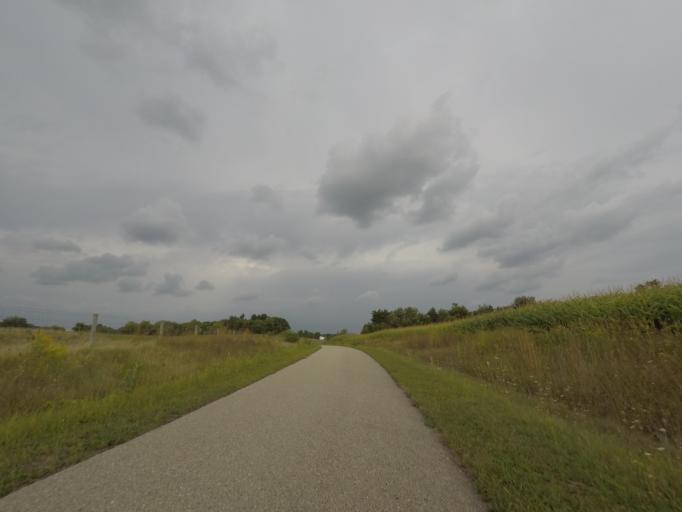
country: US
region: Wisconsin
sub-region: Jefferson County
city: Jefferson
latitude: 42.9782
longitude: -88.8225
